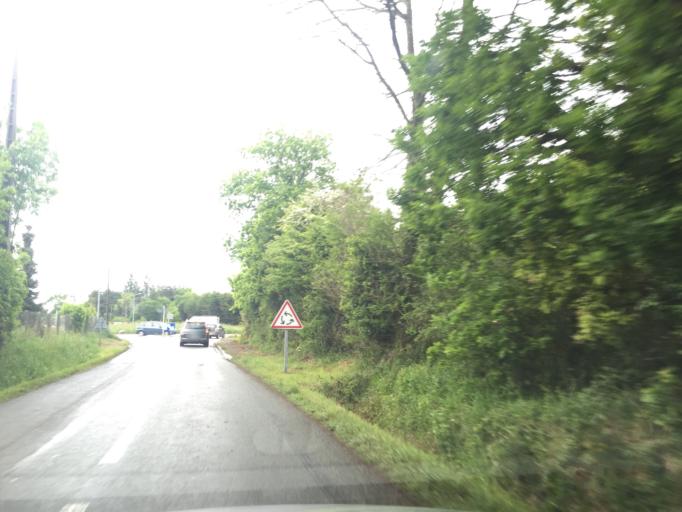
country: FR
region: Brittany
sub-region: Departement d'Ille-et-Vilaine
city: Saint-Lunaire
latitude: 48.6134
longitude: -2.1020
